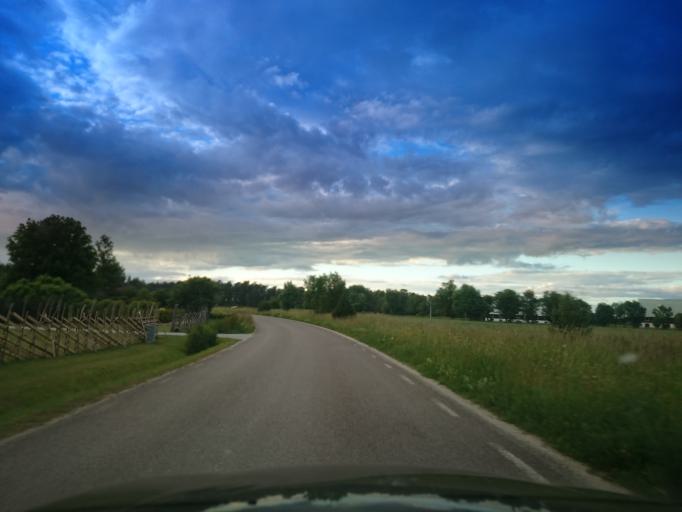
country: SE
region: Gotland
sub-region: Gotland
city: Visby
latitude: 57.5354
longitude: 18.3919
